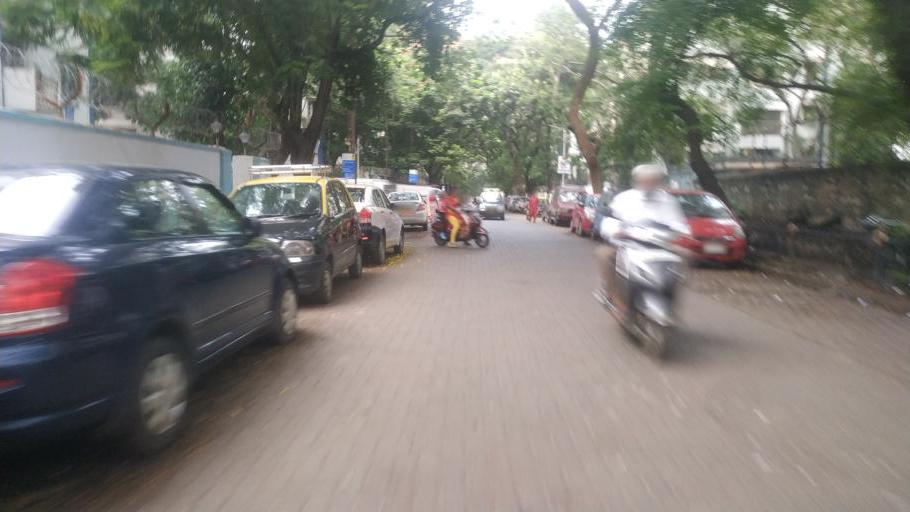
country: IN
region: Maharashtra
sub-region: Mumbai Suburban
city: Mumbai
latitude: 19.0160
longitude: 72.8566
